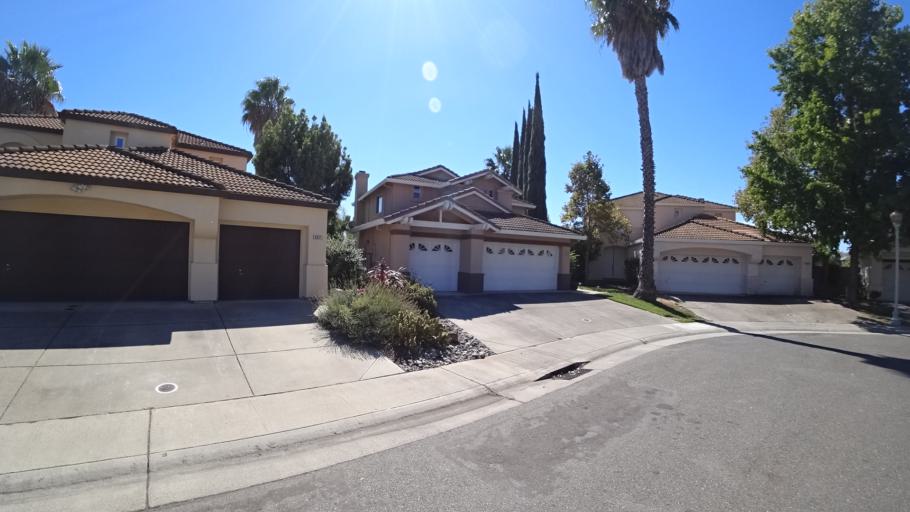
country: US
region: California
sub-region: Sacramento County
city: Laguna
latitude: 38.4197
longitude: -121.4637
